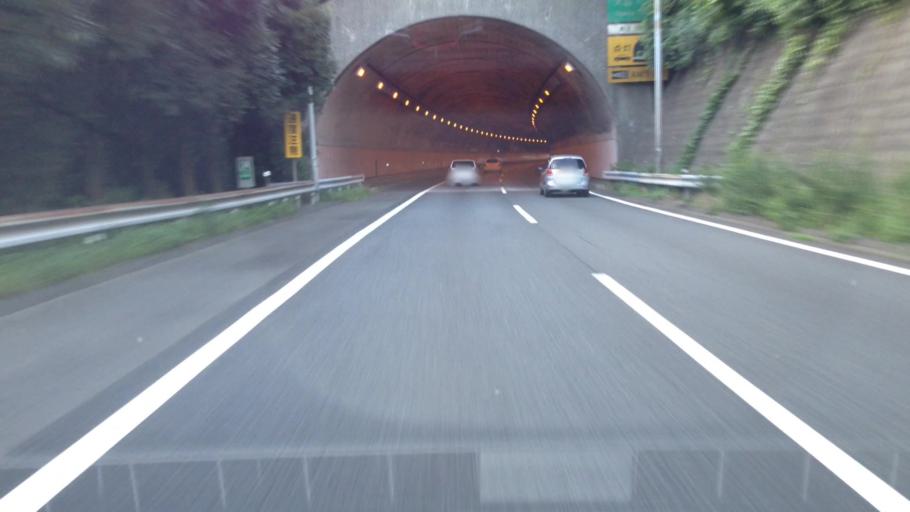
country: JP
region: Kanagawa
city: Yokosuka
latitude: 35.2845
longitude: 139.6237
